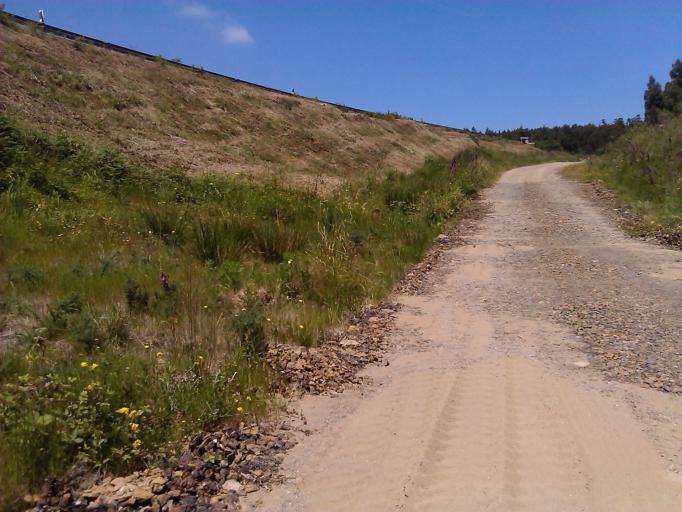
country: ES
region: Galicia
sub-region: Provincia da Coruna
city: Oroso
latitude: 42.9132
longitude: -8.4091
